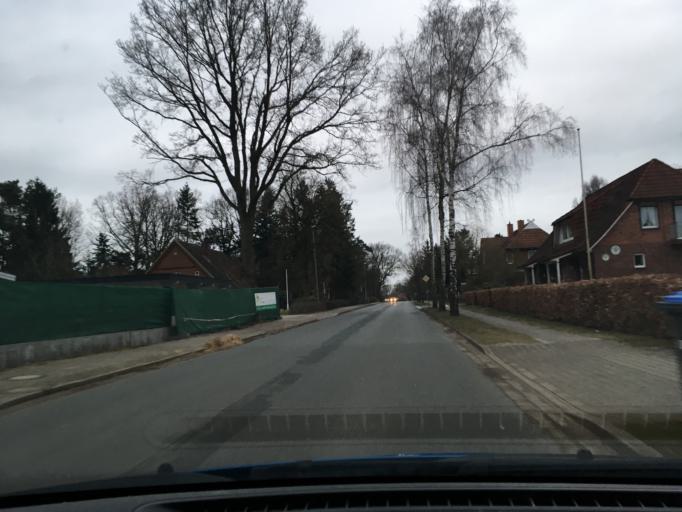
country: DE
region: Lower Saxony
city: Barum
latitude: 53.3483
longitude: 10.4077
